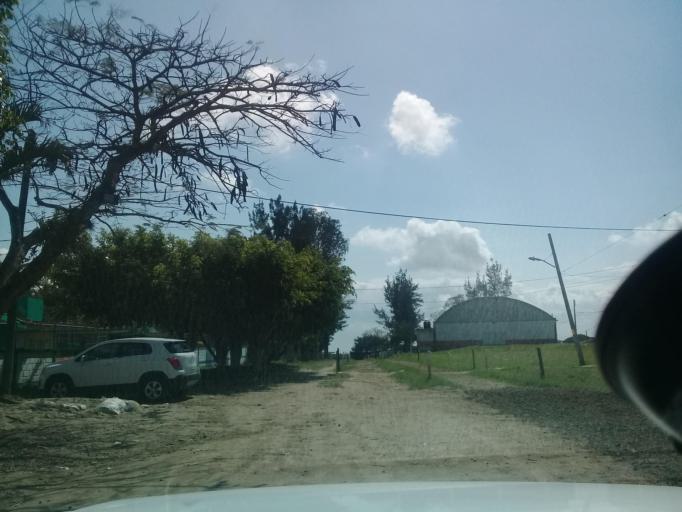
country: MX
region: Veracruz
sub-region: Coatepec
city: Bella Esperanza
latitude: 19.4376
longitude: -96.8679
